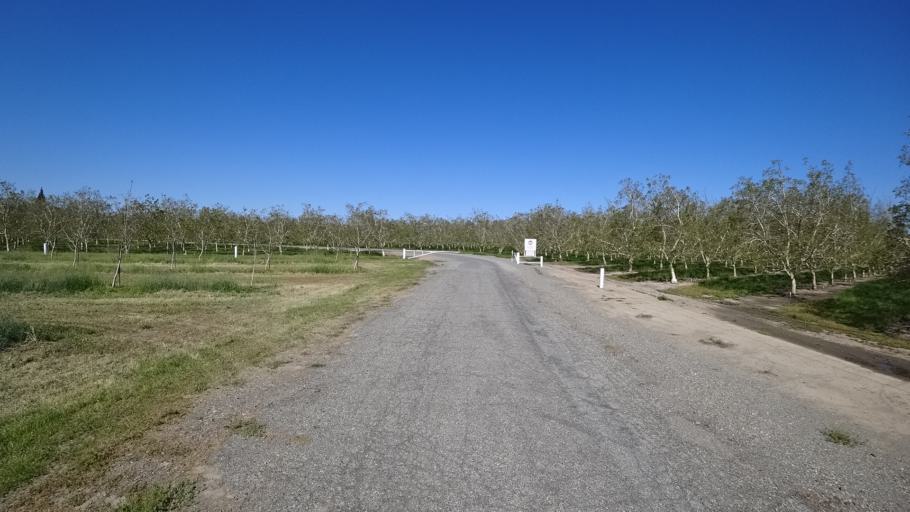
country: US
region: California
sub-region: Glenn County
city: Hamilton City
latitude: 39.7225
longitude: -122.0252
